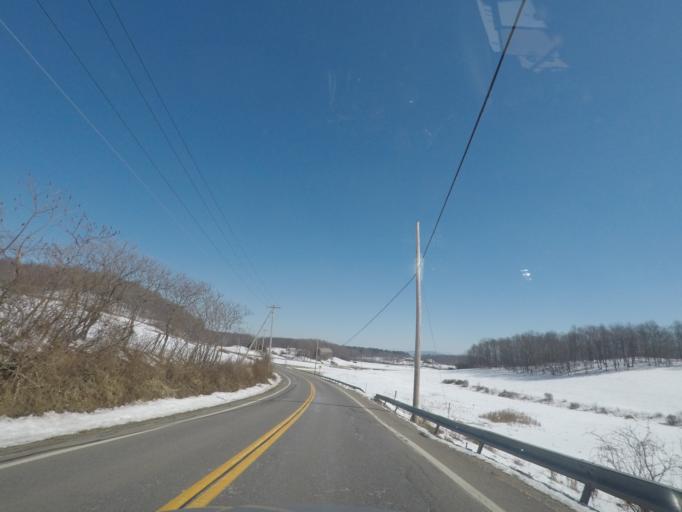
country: US
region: New York
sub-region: Saratoga County
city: Stillwater
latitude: 43.0244
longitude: -73.6659
